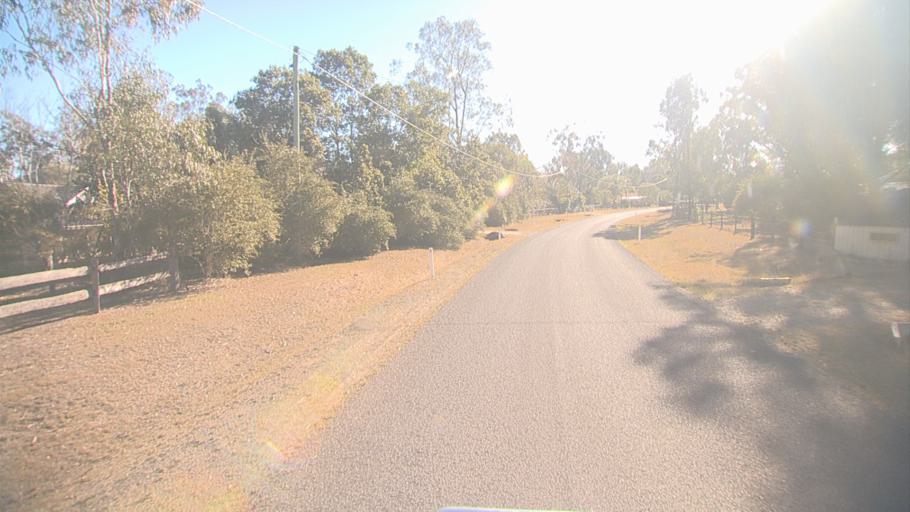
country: AU
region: Queensland
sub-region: Logan
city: North Maclean
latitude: -27.8283
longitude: 152.9901
